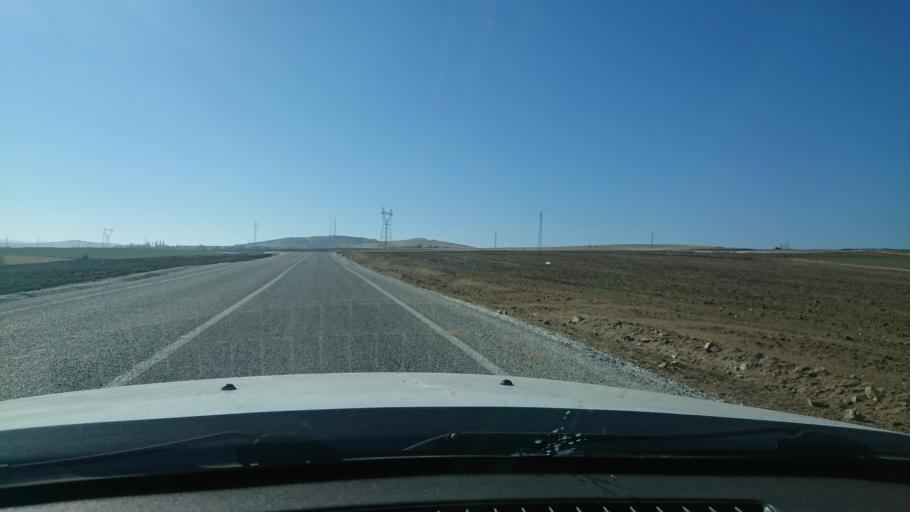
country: TR
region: Aksaray
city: Agacoren
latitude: 38.8970
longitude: 33.9316
